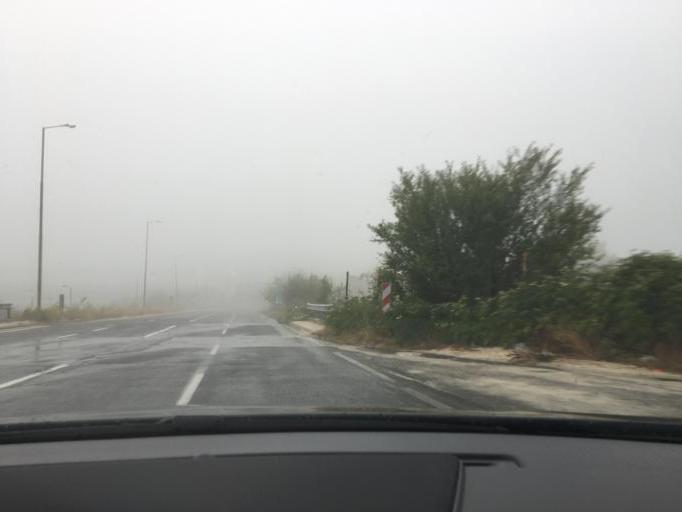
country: MK
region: Kriva Palanka
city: Kriva Palanka
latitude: 42.2204
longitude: 22.4559
